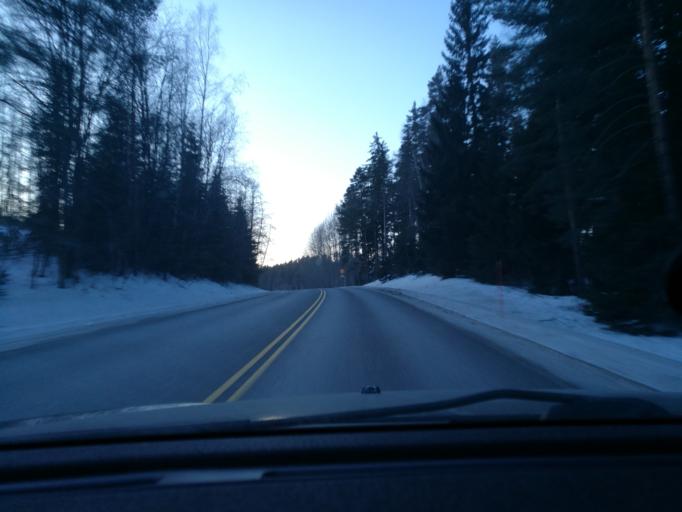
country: FI
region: Uusimaa
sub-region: Helsinki
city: Vihti
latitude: 60.4353
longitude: 24.4172
